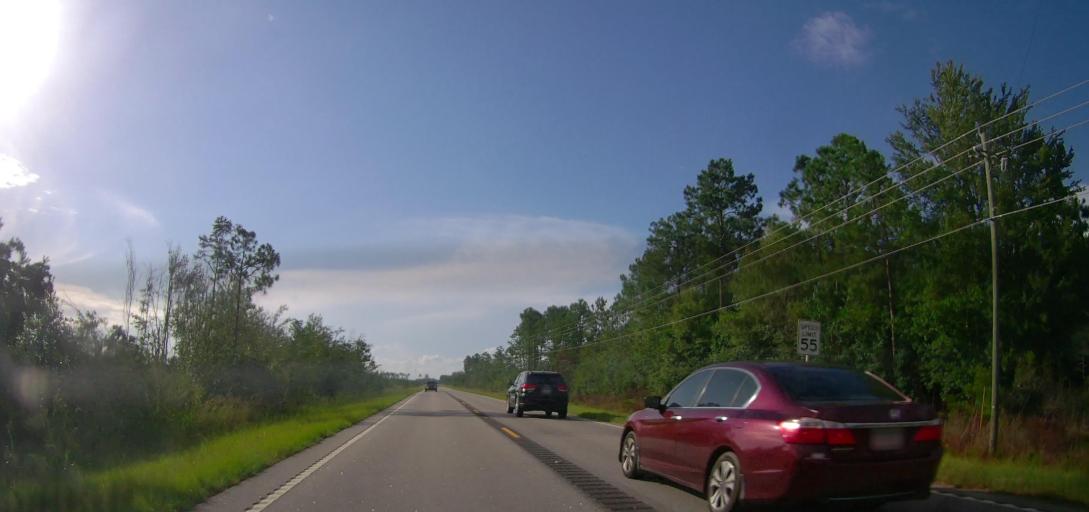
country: US
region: Georgia
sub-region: Coffee County
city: Nicholls
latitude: 31.3663
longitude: -82.6291
